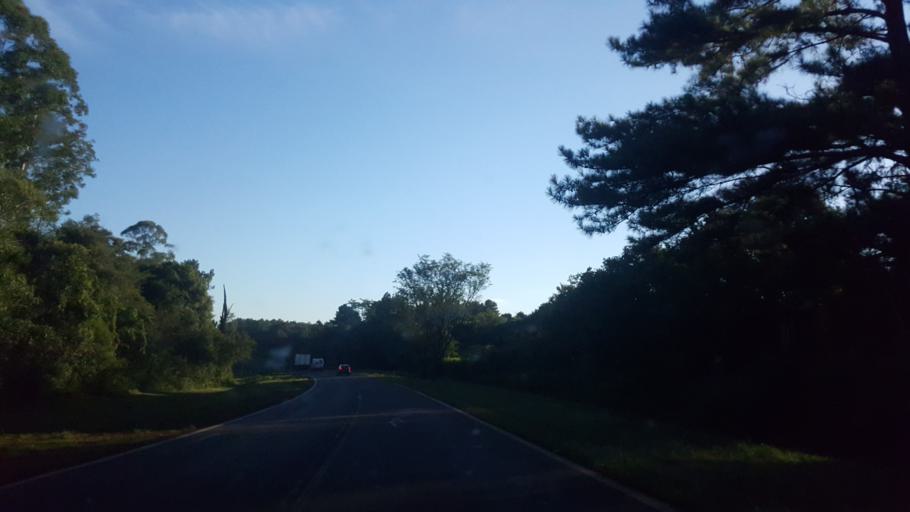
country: AR
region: Misiones
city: El Alcazar
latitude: -26.7323
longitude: -54.8738
